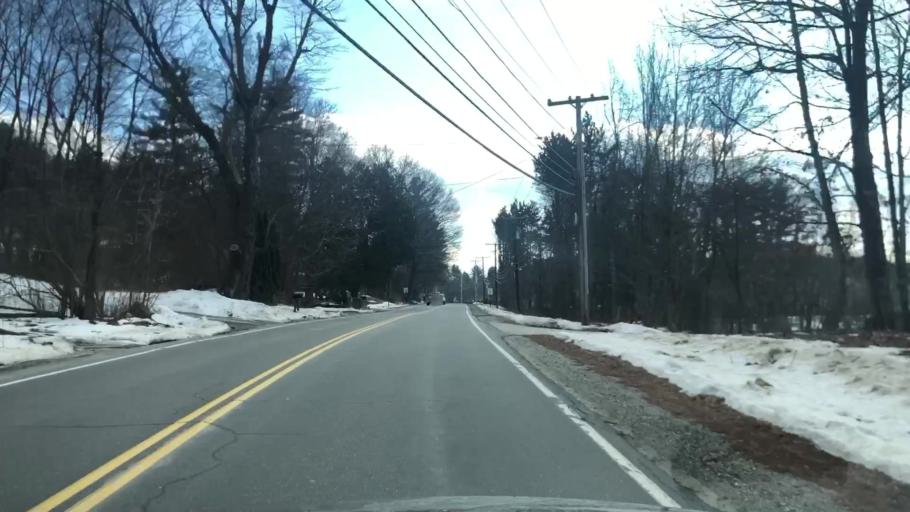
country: US
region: New Hampshire
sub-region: Hillsborough County
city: Milford
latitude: 42.8445
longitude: -71.6596
